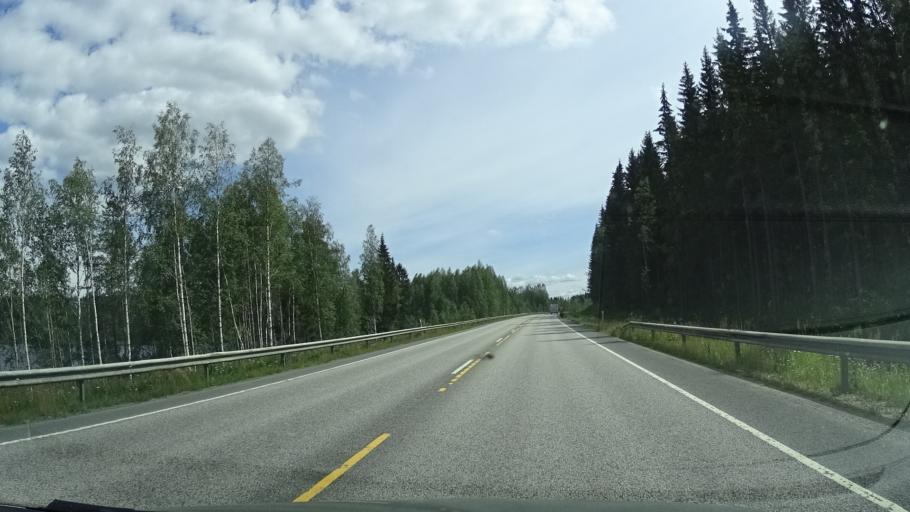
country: FI
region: Central Finland
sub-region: Jyvaeskylae
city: Jyvaeskylae
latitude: 62.2566
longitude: 25.6176
